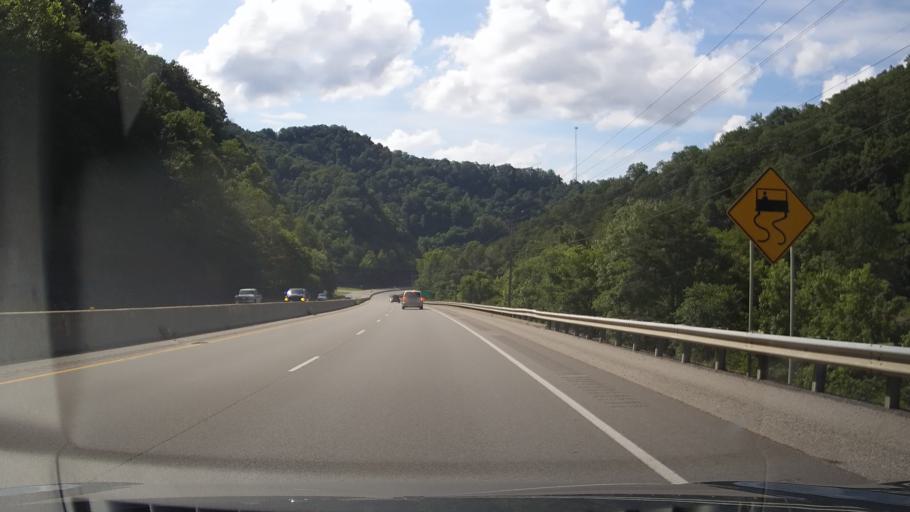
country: US
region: Kentucky
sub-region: Floyd County
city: Prestonsburg
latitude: 37.6468
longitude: -82.7795
